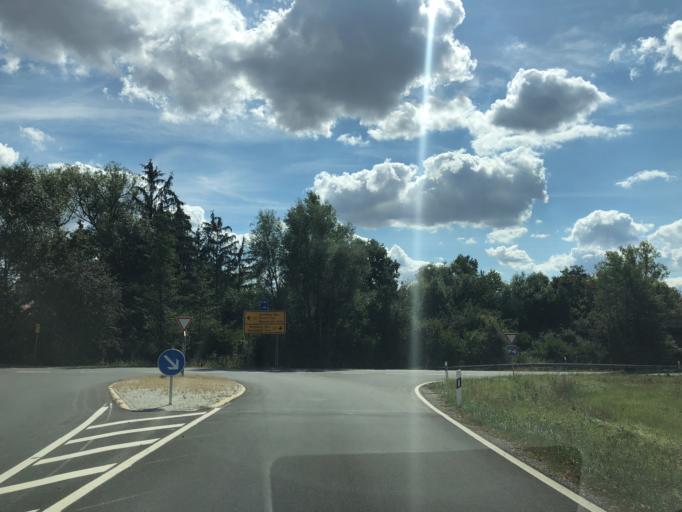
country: DE
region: Bavaria
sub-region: Regierungsbezirk Unterfranken
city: Prichsenstadt
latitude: 49.8448
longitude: 10.3517
